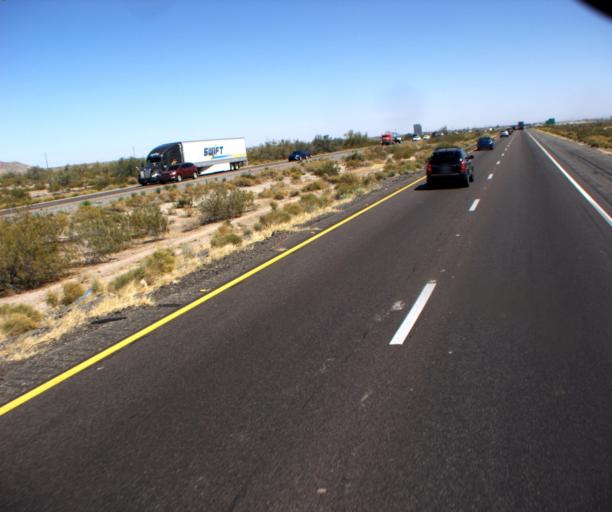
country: US
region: Arizona
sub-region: Maricopa County
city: Buckeye
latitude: 33.4524
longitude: -112.5320
